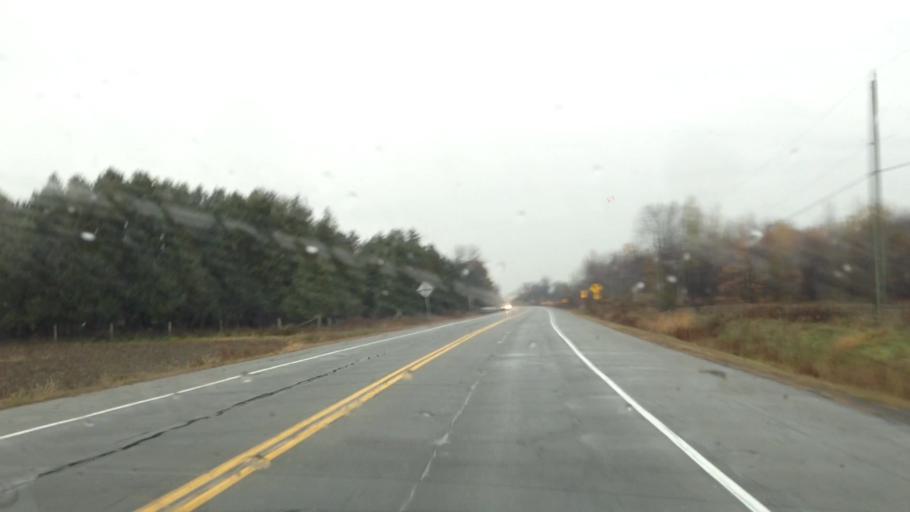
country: CA
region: Ontario
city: Clarence-Rockland
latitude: 45.3447
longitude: -75.3653
